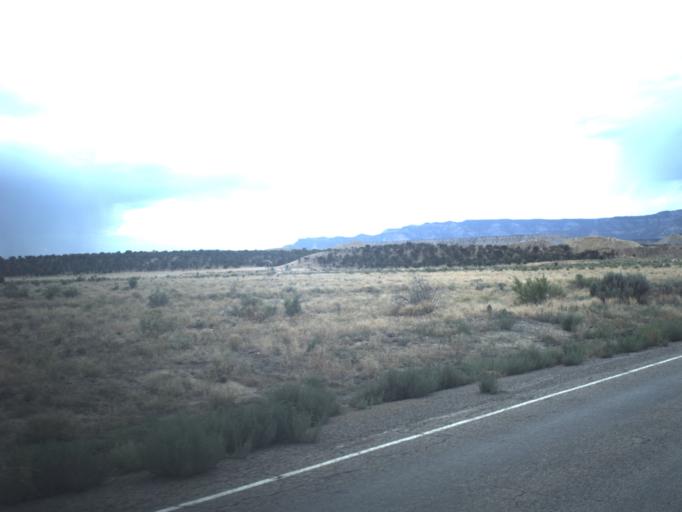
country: US
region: Utah
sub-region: Carbon County
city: Price
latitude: 39.4842
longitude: -110.8922
